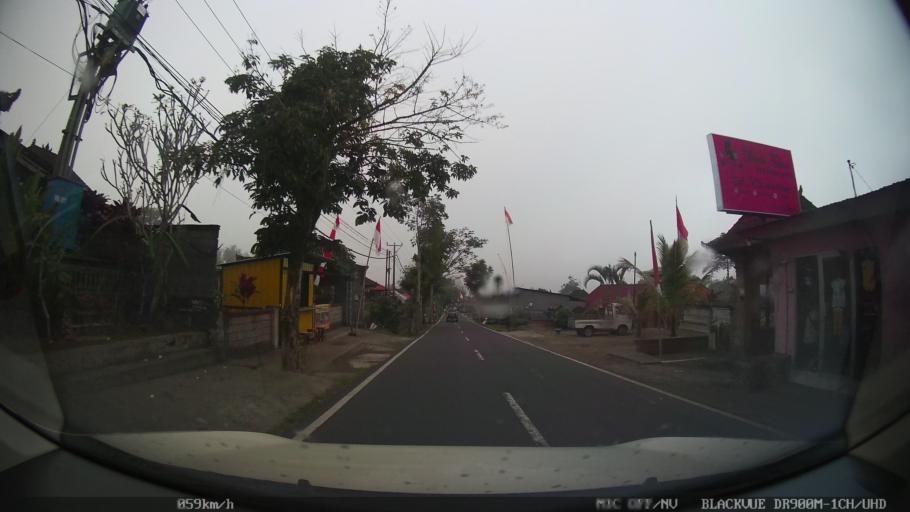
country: ID
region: Bali
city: Banjar Kedisan
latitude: -8.3054
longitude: 115.3067
